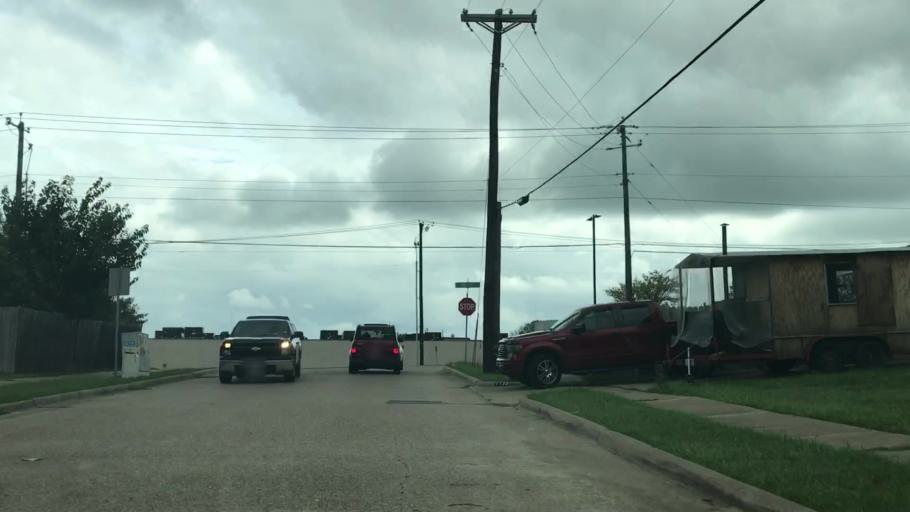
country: US
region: Texas
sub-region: Dallas County
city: Garland
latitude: 32.8947
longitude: -96.6157
